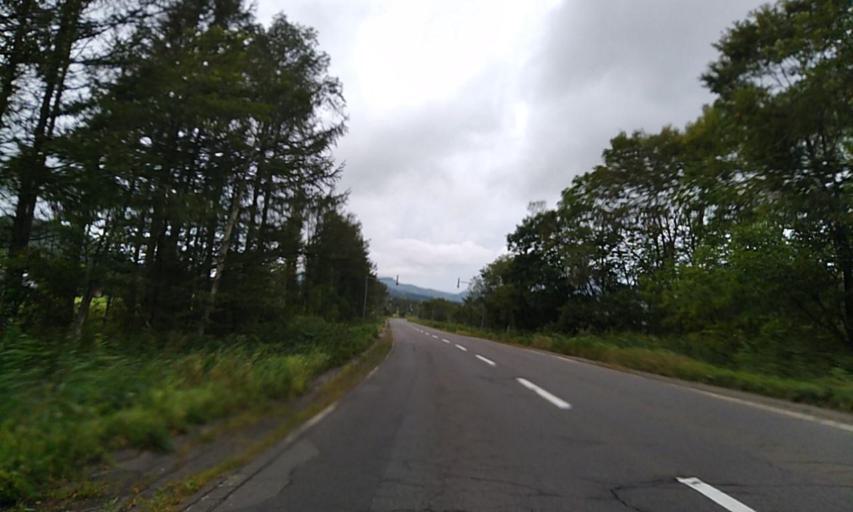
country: JP
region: Hokkaido
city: Bihoro
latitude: 43.5242
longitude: 144.4167
